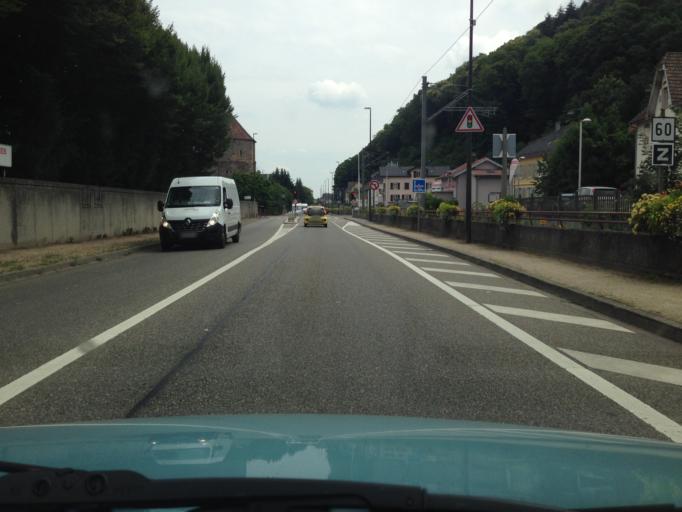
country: FR
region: Alsace
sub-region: Departement du Haut-Rhin
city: Thann
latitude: 47.8130
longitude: 7.0947
